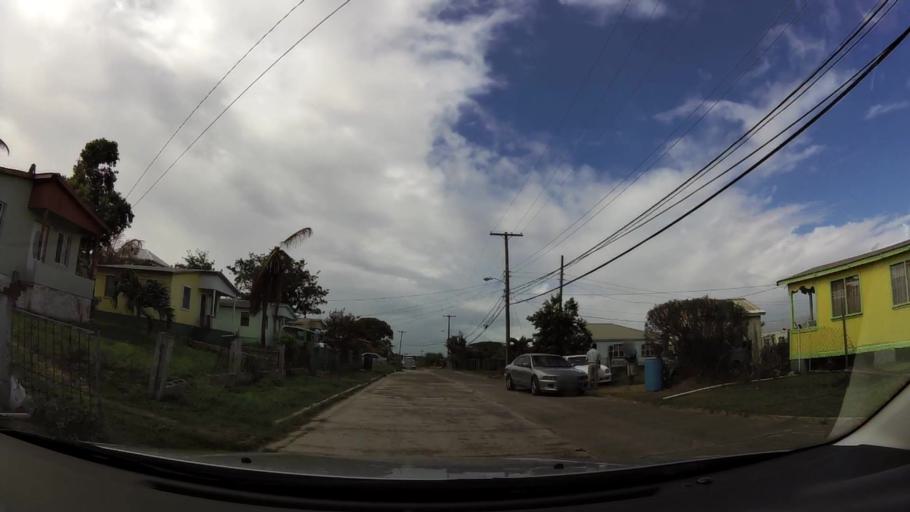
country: AG
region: Saint George
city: Piggotts
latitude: 17.1107
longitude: -61.8147
